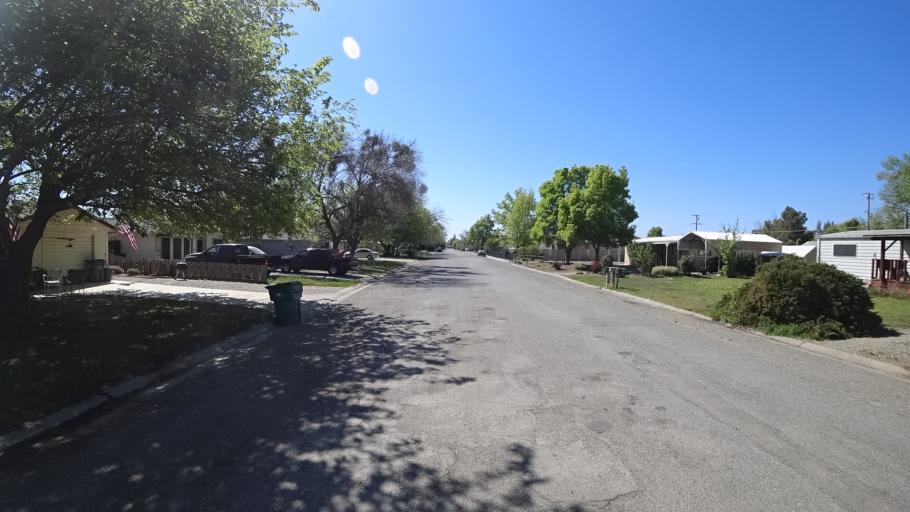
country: US
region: California
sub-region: Glenn County
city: Willows
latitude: 39.5289
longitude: -122.1880
